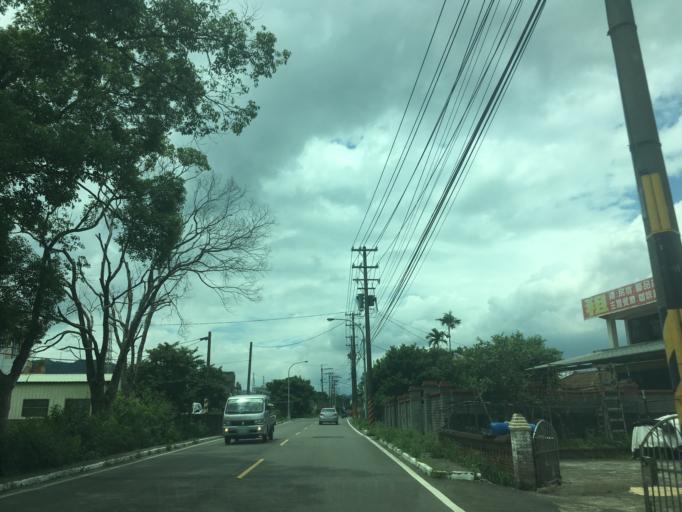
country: TW
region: Taiwan
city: Daxi
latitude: 24.8572
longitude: 121.2941
